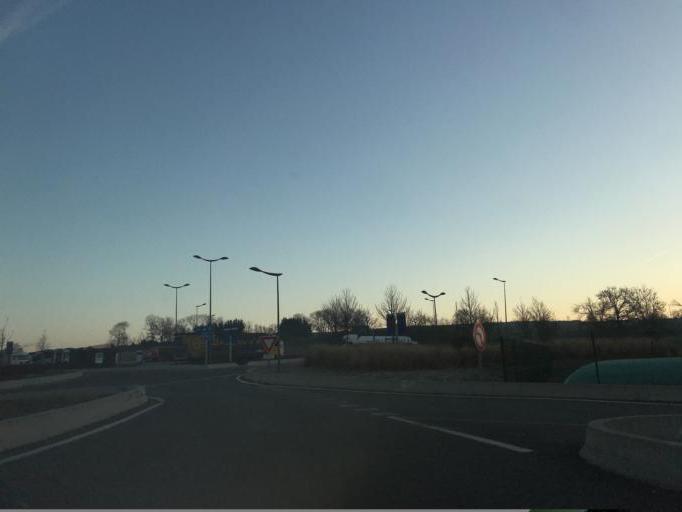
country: FR
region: Rhone-Alpes
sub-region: Departement de la Loire
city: Bussieres
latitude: 45.8515
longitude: 4.2256
